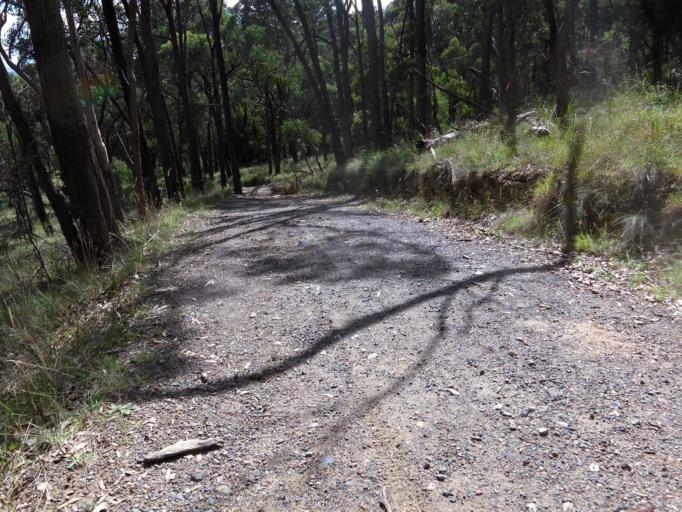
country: AU
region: Victoria
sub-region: Knox
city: The Basin
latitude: -37.8361
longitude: 145.3356
